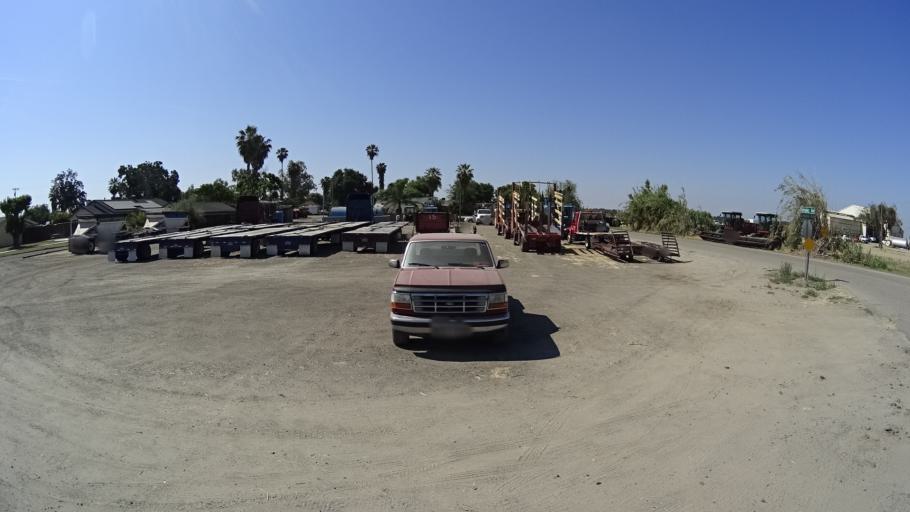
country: US
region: California
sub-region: Kings County
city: Lemoore
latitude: 36.3424
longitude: -119.8107
